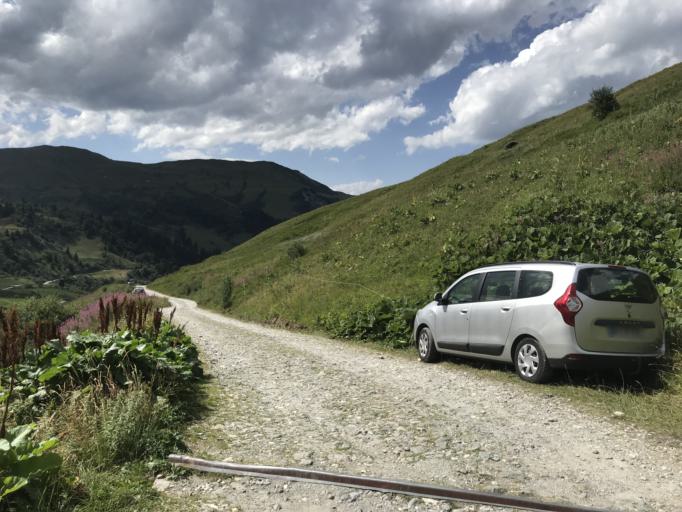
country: FR
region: Rhone-Alpes
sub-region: Departement de la Savoie
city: Beaufort
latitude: 45.6607
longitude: 6.6328
